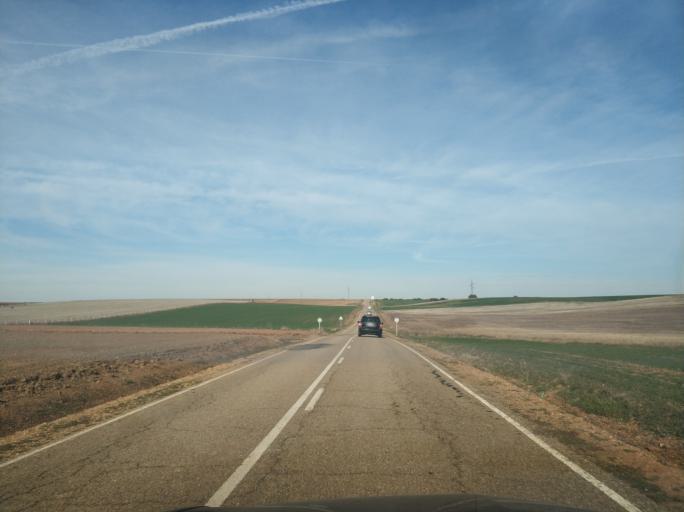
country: ES
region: Castille and Leon
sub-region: Provincia de Salamanca
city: Parada de Arriba
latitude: 40.9903
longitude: -5.8022
